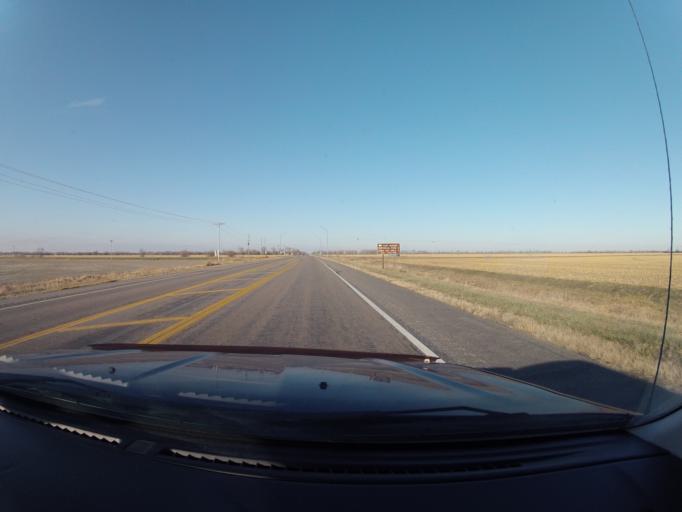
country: US
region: Nebraska
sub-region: Kearney County
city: Minden
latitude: 40.6393
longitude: -98.9514
